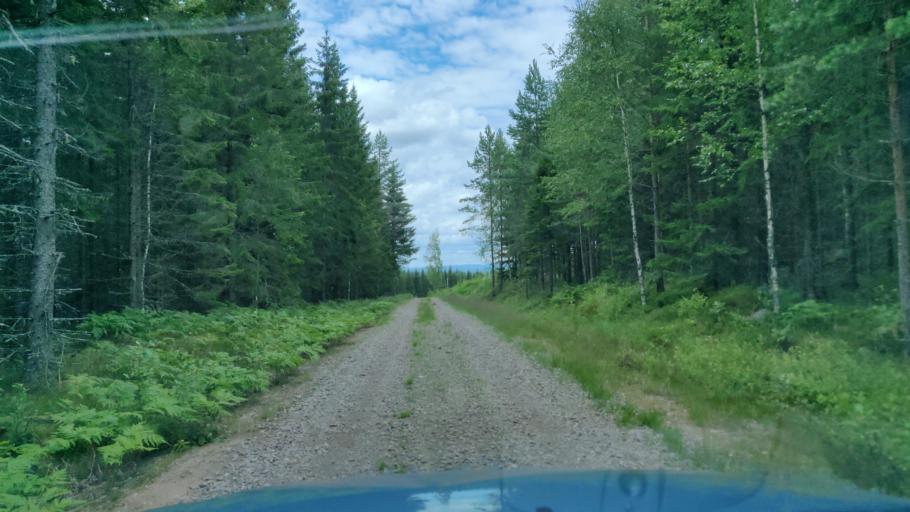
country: SE
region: Vaermland
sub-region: Hagfors Kommun
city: Hagfors
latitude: 59.9663
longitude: 13.5845
